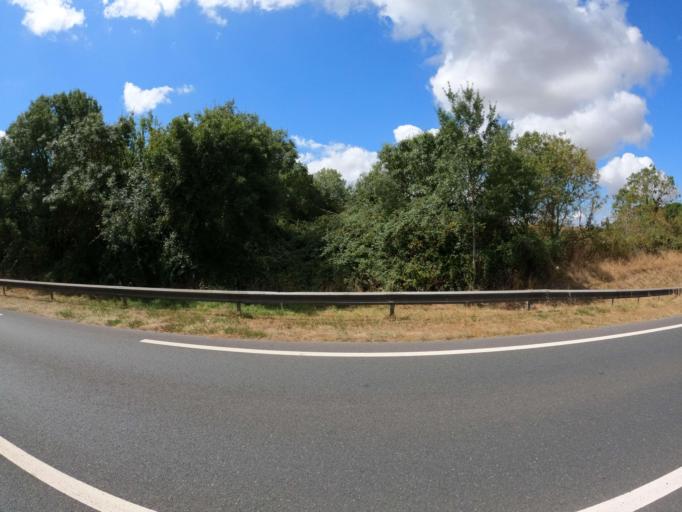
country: FR
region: Pays de la Loire
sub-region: Departement de la Loire-Atlantique
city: Ancenis
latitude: 47.3760
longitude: -1.1692
